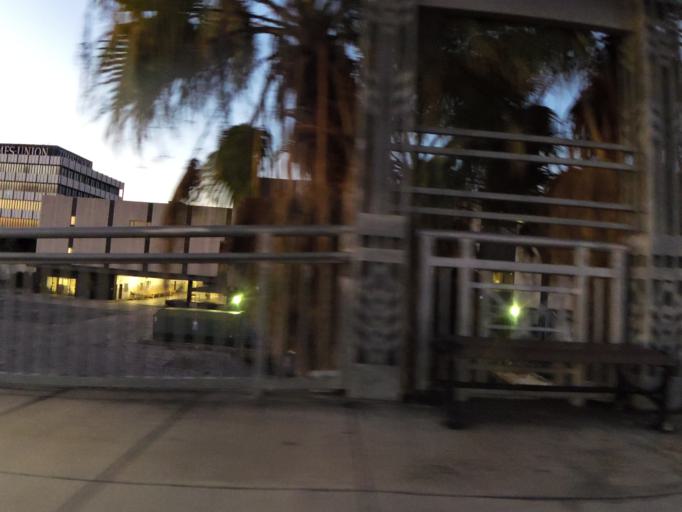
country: US
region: Florida
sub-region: Duval County
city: Jacksonville
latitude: 30.3237
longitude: -81.6669
